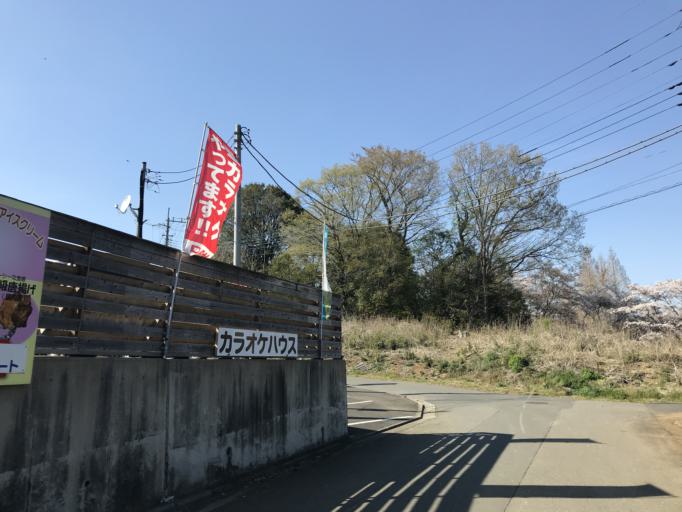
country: JP
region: Ibaraki
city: Moriya
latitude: 35.9603
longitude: 139.9575
